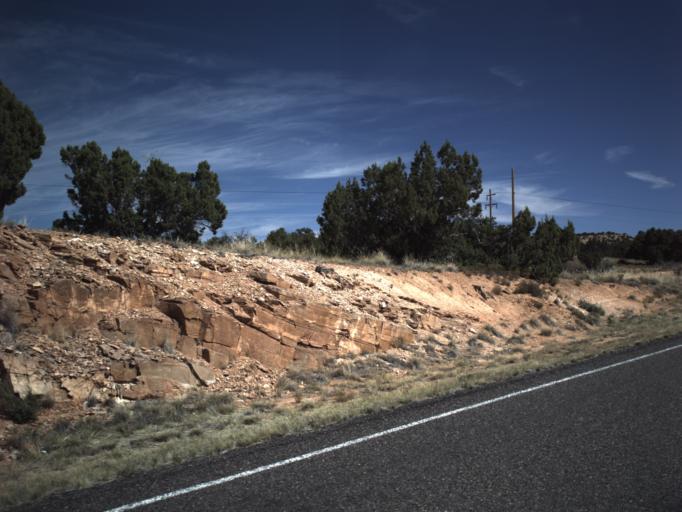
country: US
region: Utah
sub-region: Wayne County
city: Loa
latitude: 37.7485
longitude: -111.4908
